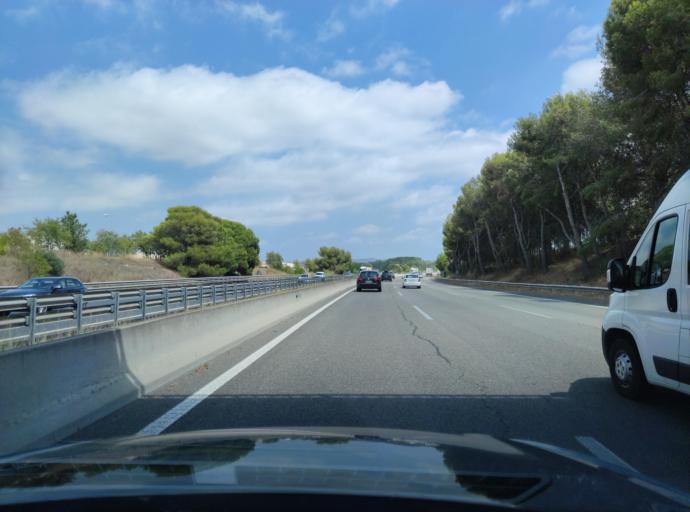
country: ES
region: Catalonia
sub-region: Provincia de Barcelona
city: Vilafranca del Penedes
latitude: 41.3305
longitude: 1.6643
